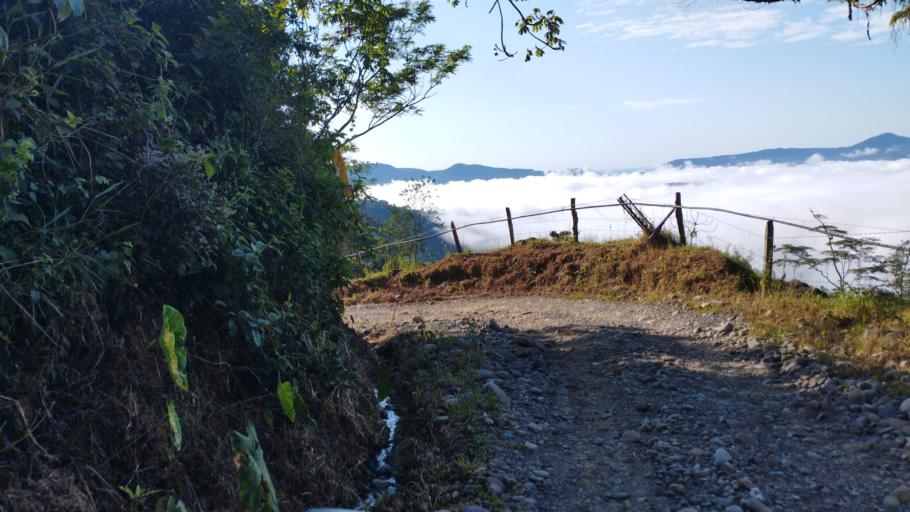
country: CO
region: Boyaca
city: San Luis de Gaceno
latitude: 4.7884
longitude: -73.0955
